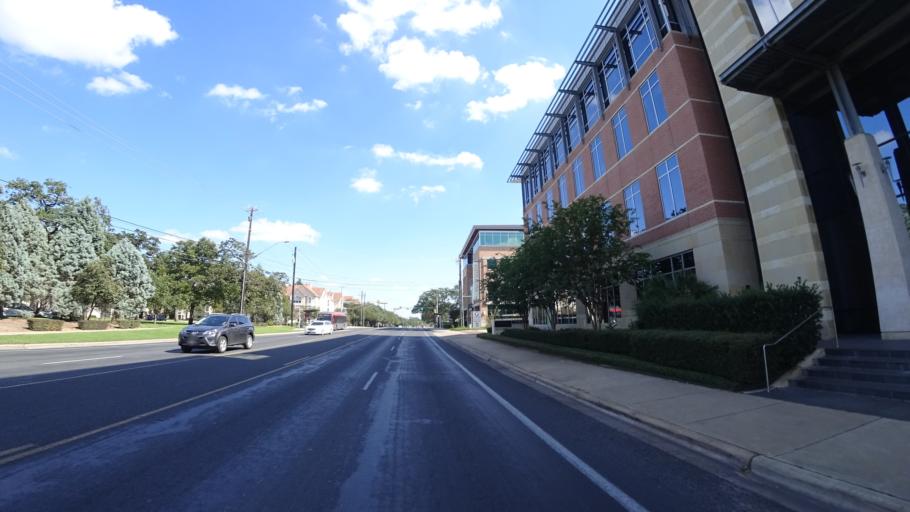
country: US
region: Texas
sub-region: Travis County
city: Austin
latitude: 30.3048
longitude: -97.7424
